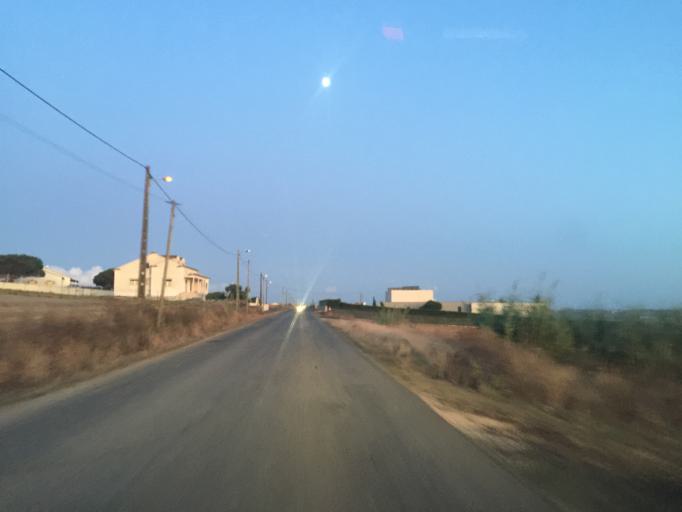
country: PT
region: Leiria
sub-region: Peniche
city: Atouguia da Baleia
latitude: 39.2903
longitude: -9.3074
